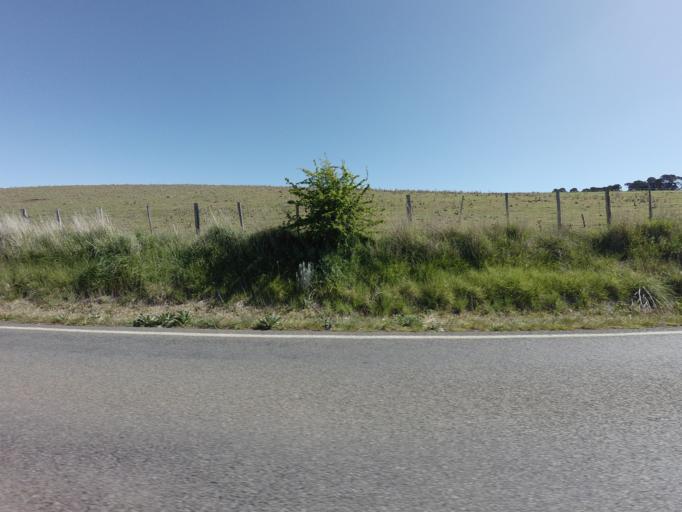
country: AU
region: Tasmania
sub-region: Derwent Valley
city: New Norfolk
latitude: -42.6356
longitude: 146.9164
